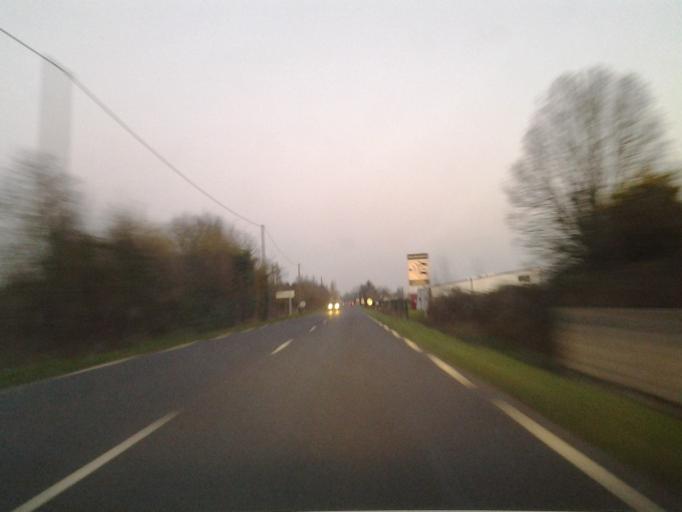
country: FR
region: Pays de la Loire
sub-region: Departement de la Vendee
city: Sallertaine
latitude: 46.8720
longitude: -1.9415
